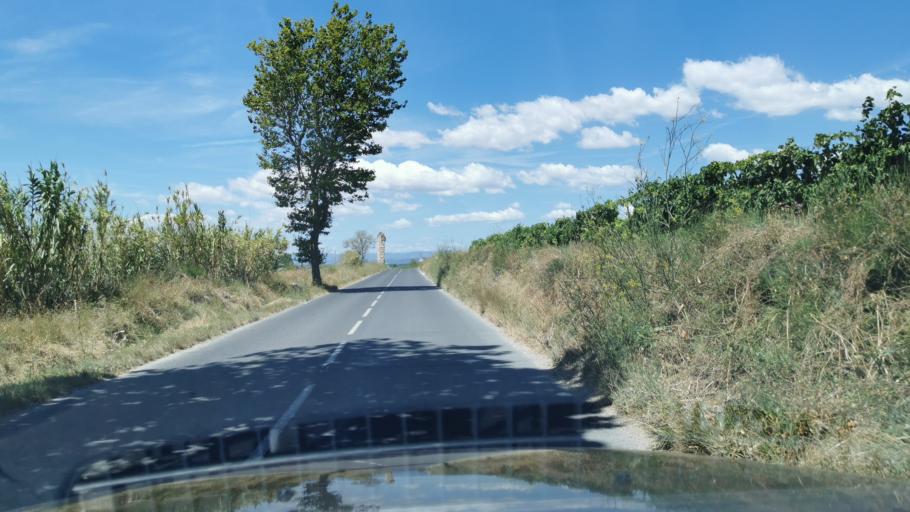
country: FR
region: Languedoc-Roussillon
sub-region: Departement de l'Aude
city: Vinassan
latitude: 43.1915
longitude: 3.0817
